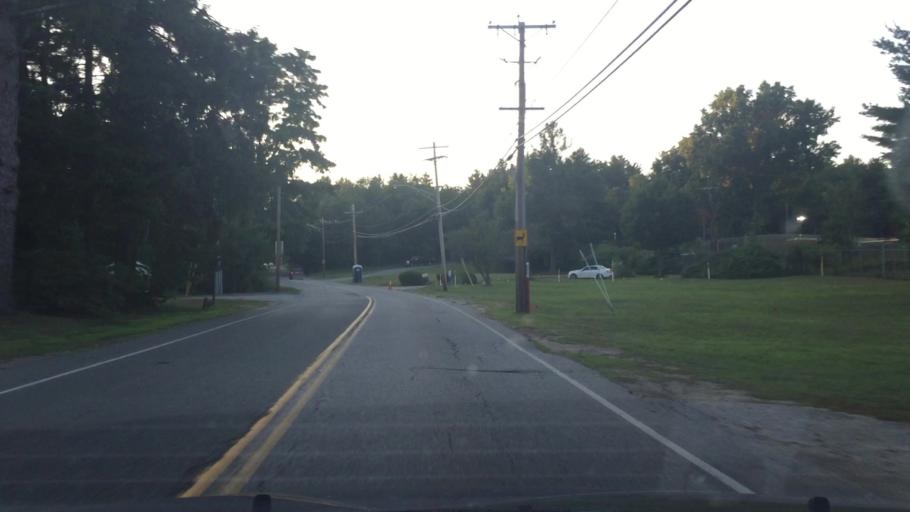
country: US
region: New Hampshire
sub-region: Rockingham County
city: Plaistow
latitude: 42.8072
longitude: -71.0860
